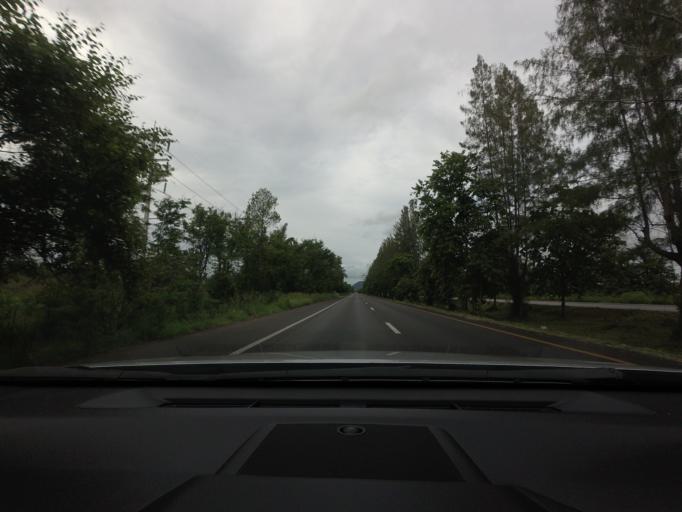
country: TH
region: Prachuap Khiri Khan
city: Hua Hin
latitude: 12.6572
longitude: 99.8737
